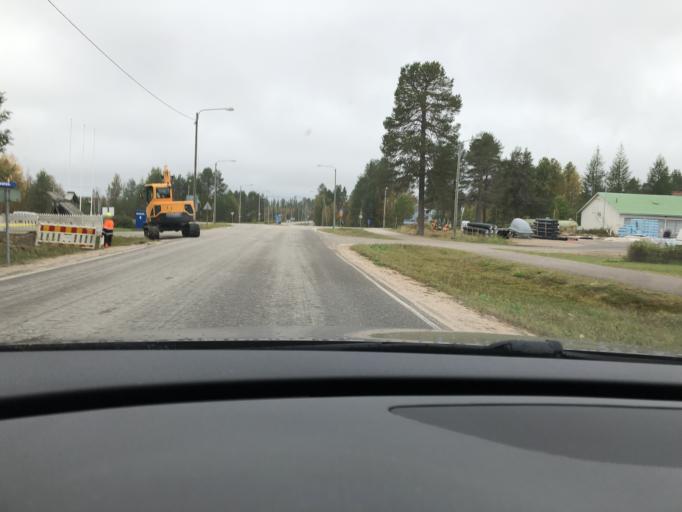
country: FI
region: Lapland
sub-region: Itae-Lappi
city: Posio
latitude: 66.1098
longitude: 28.1776
